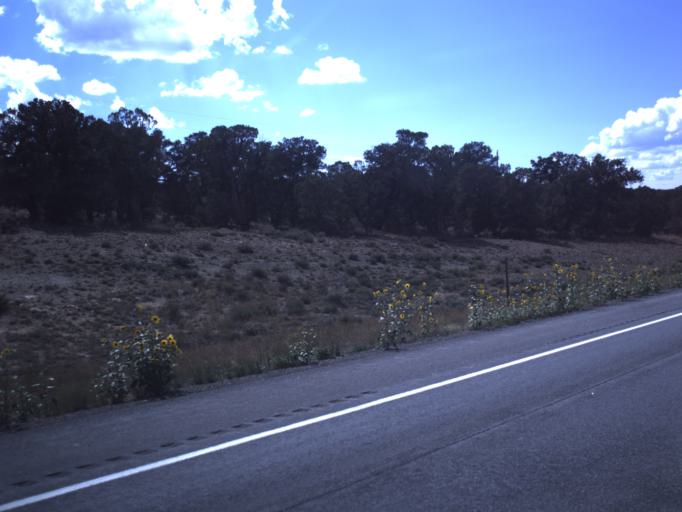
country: US
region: Utah
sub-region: Duchesne County
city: Duchesne
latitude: 40.1902
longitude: -110.6777
